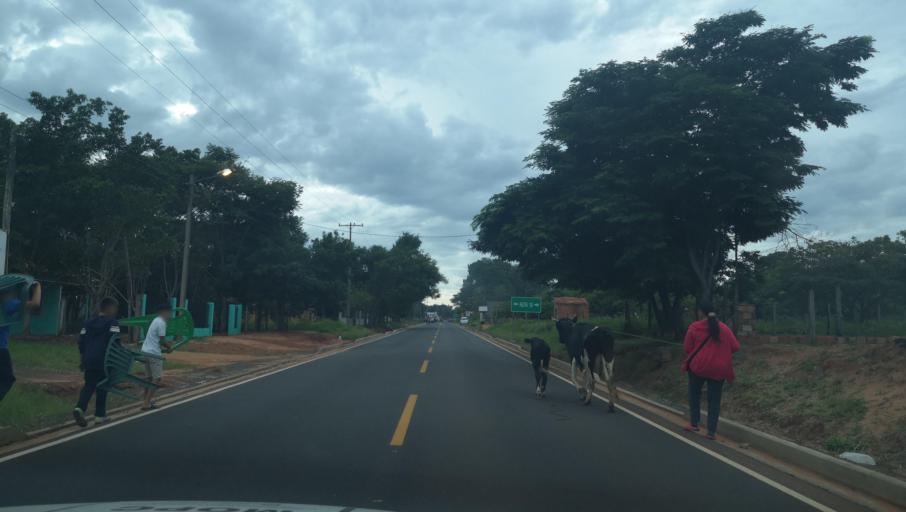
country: PY
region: San Pedro
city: Capiibary
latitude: -24.7445
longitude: -56.0299
